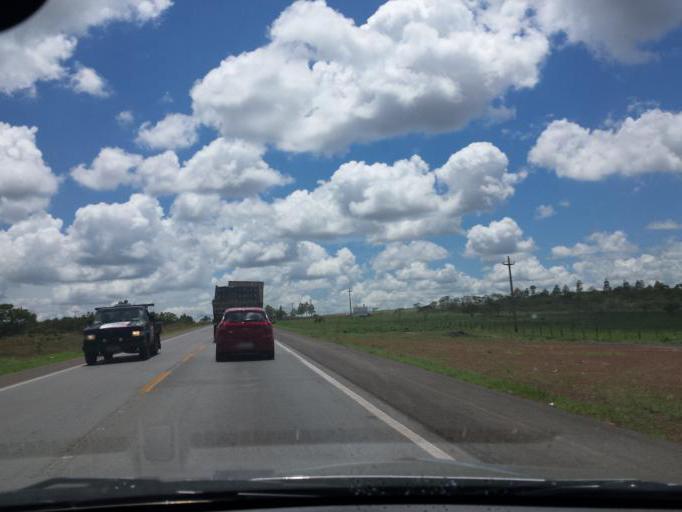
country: BR
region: Goias
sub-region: Cristalina
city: Cristalina
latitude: -16.7276
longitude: -47.6343
